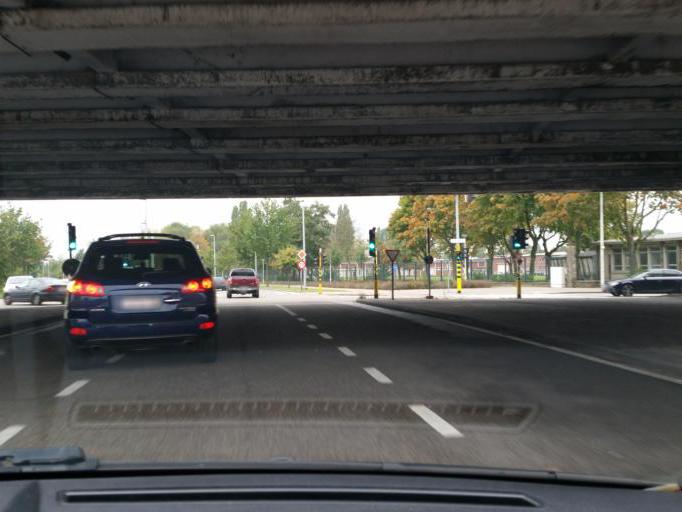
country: BE
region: Flanders
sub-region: Provincie Antwerpen
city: Aartselaar
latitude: 51.1731
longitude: 4.3880
